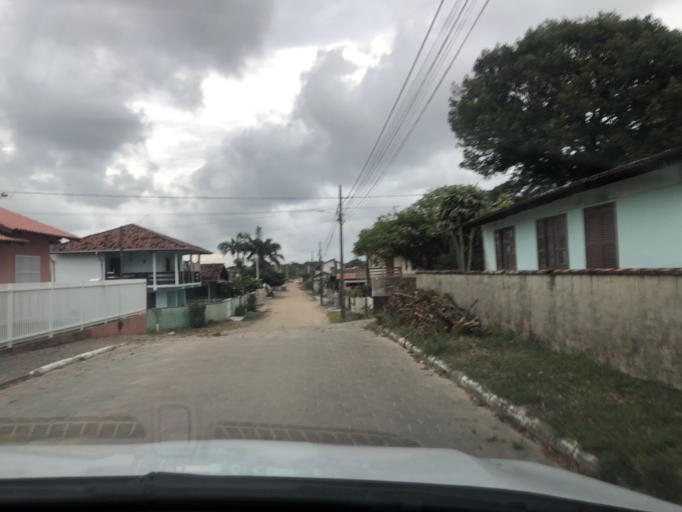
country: BR
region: Santa Catarina
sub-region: Sao Francisco Do Sul
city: Sao Francisco do Sul
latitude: -26.2256
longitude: -48.5207
